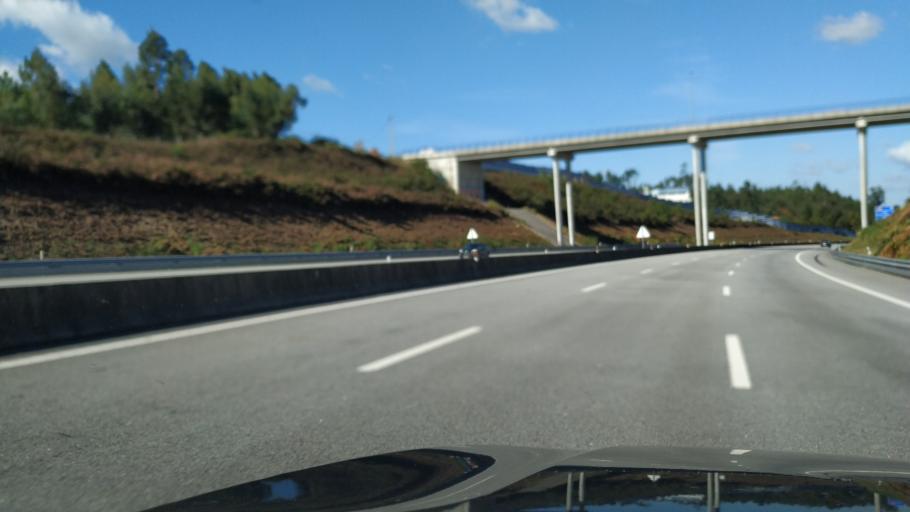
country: PT
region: Porto
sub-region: Vila Nova de Gaia
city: Olival
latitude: 41.0805
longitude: -8.5485
